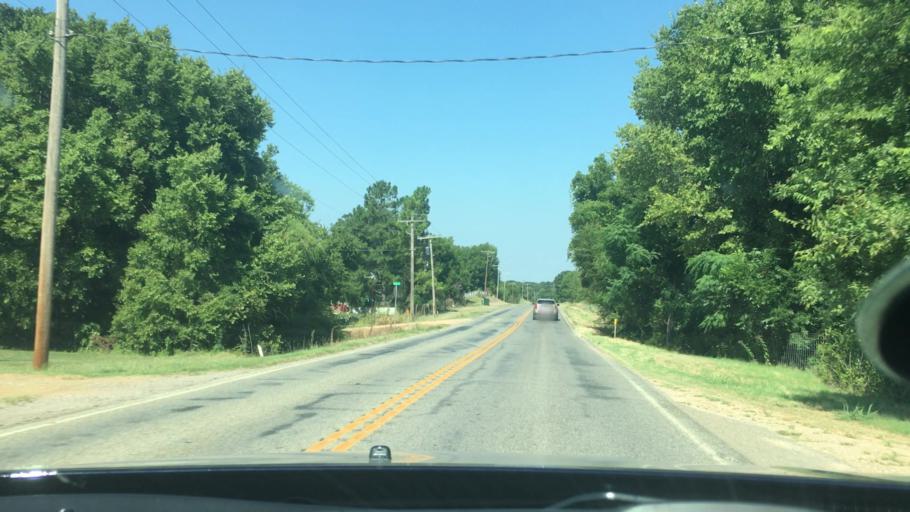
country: US
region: Oklahoma
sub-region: Johnston County
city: Tishomingo
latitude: 34.2378
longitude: -96.6005
